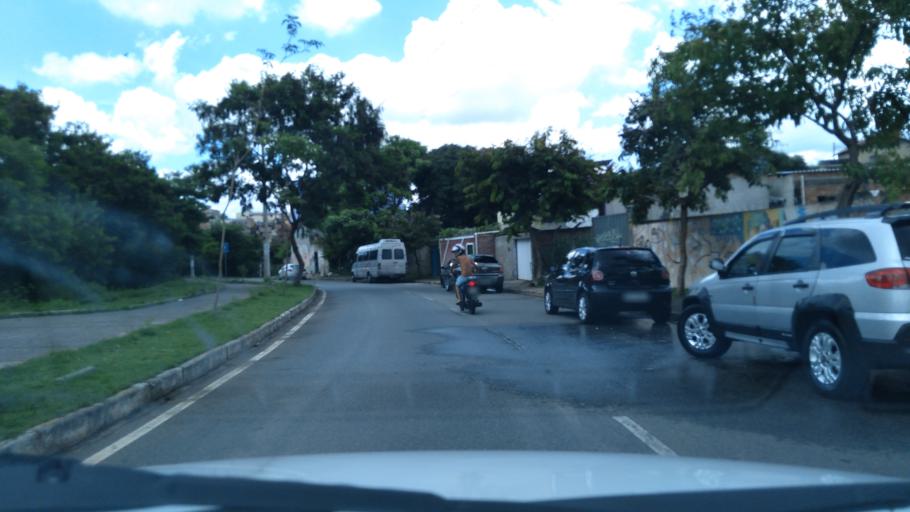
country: BR
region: Minas Gerais
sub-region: Belo Horizonte
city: Belo Horizonte
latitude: -19.9171
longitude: -43.9020
